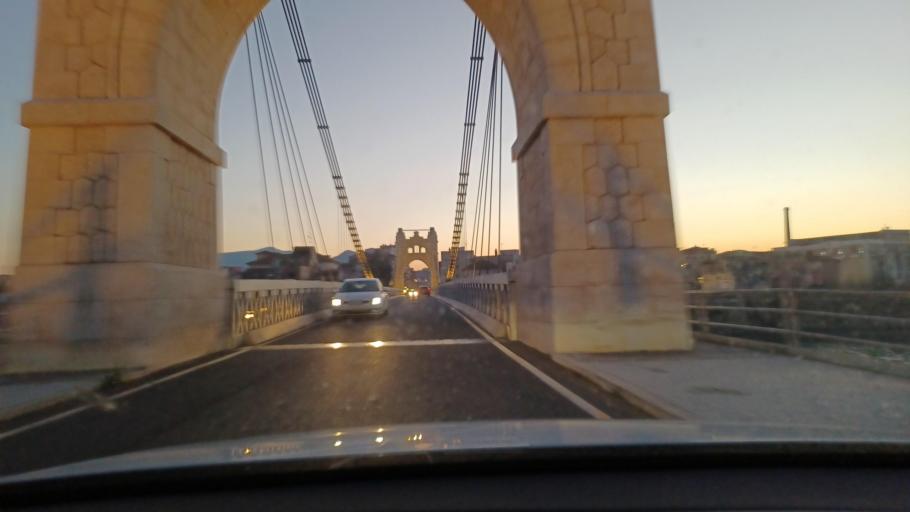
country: ES
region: Catalonia
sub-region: Provincia de Tarragona
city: Amposta
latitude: 40.7155
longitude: 0.5823
